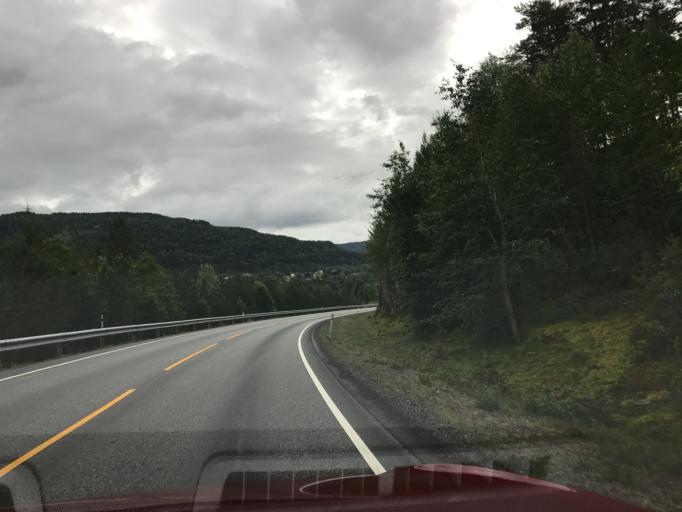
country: NO
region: Buskerud
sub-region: Rollag
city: Rollag
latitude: 60.0384
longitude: 9.2191
